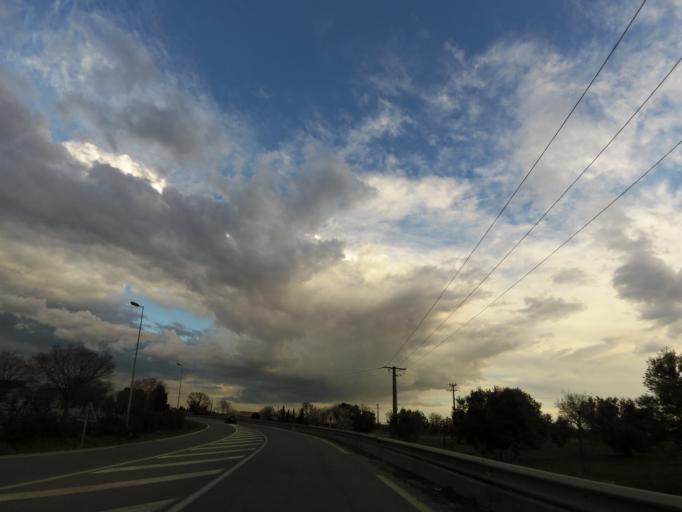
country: FR
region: Languedoc-Roussillon
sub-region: Departement du Gard
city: Codognan
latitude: 43.7270
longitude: 4.2415
